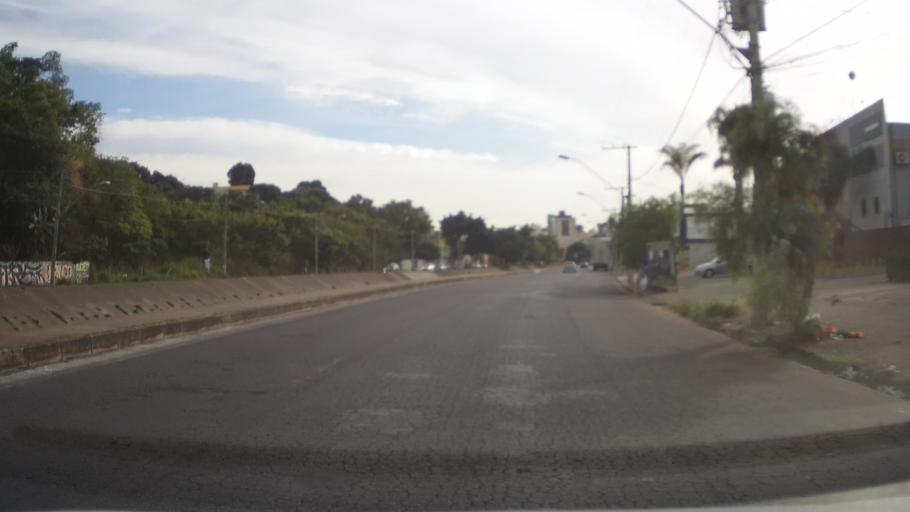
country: BR
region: Minas Gerais
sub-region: Contagem
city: Contagem
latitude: -19.8765
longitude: -44.0038
